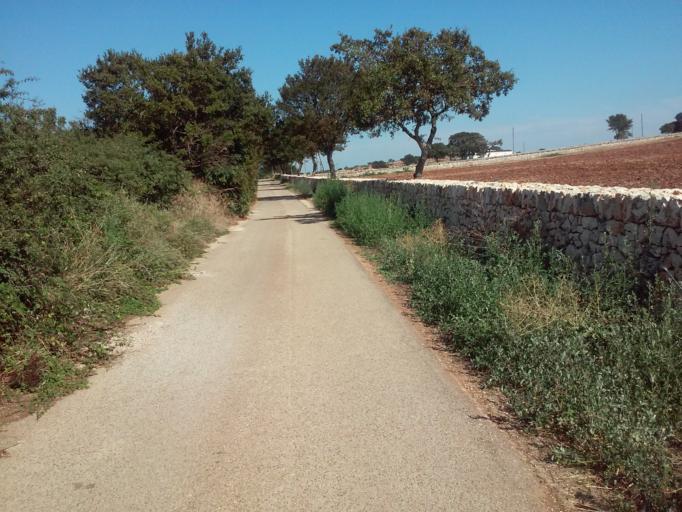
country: IT
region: Apulia
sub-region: Provincia di Bari
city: Sammichele di Bari
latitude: 40.8214
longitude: 17.0174
